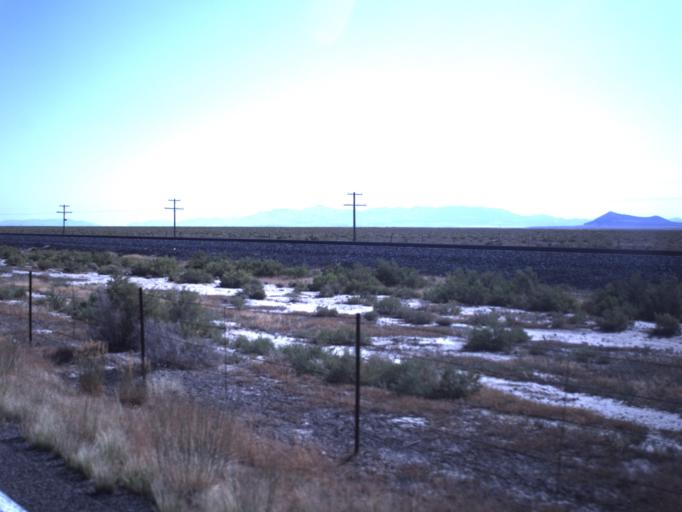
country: US
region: Utah
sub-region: Millard County
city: Delta
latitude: 39.0776
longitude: -112.7566
